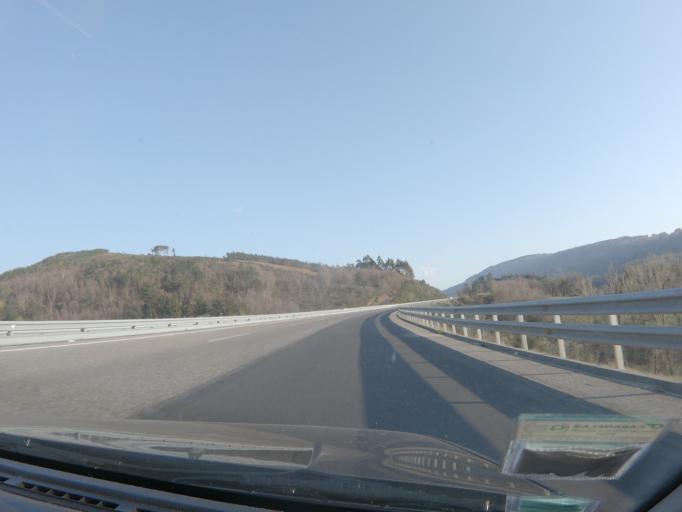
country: ES
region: Galicia
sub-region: Provincia de Lugo
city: Becerrea
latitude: 42.9083
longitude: -7.1919
